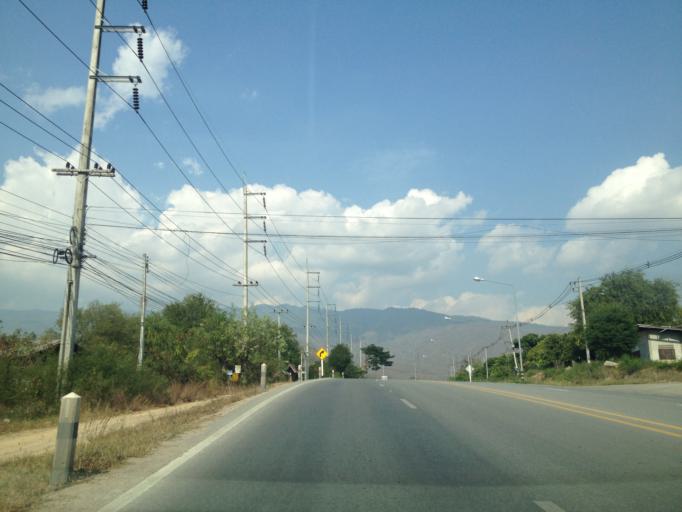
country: TH
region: Chiang Mai
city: Hot
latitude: 18.2979
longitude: 98.6424
